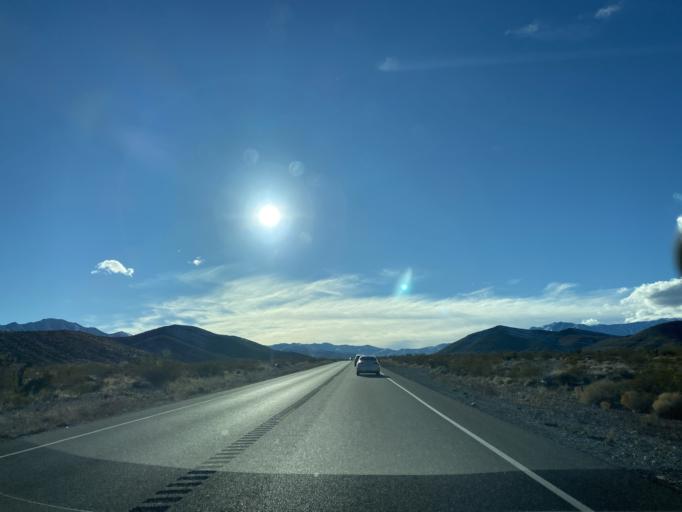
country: US
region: Nevada
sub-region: Clark County
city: Summerlin South
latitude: 36.2944
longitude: -115.4223
